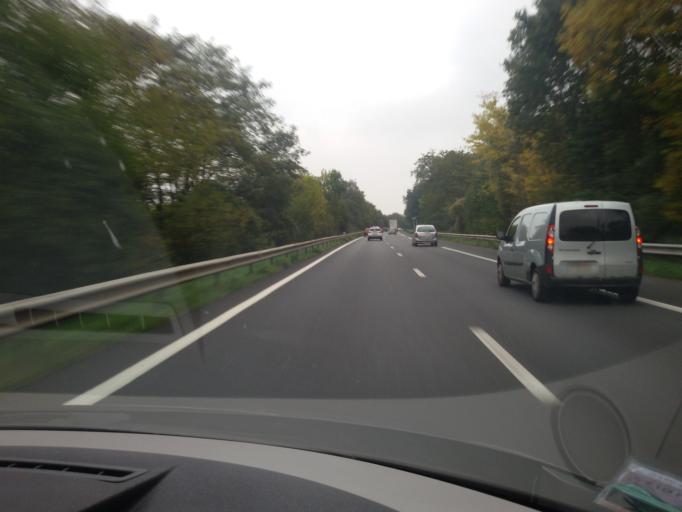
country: FR
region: Ile-de-France
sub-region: Departement de l'Essonne
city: Marcoussis
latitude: 48.6348
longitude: 2.2152
